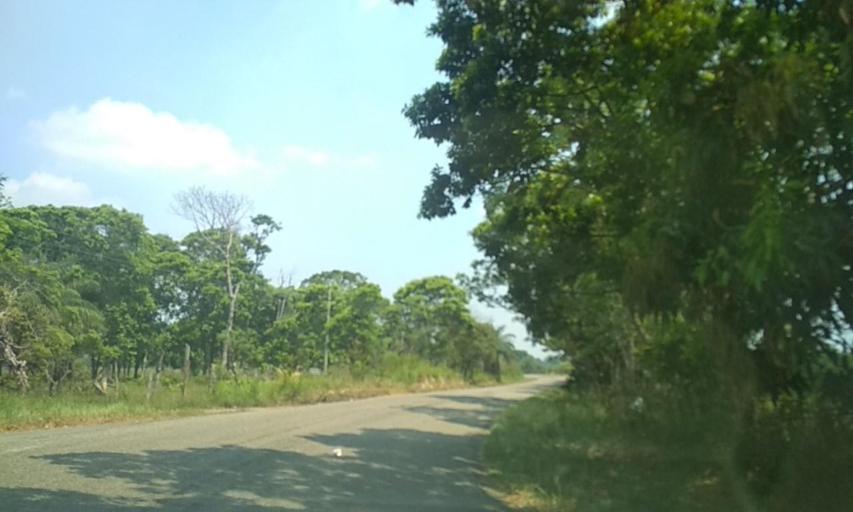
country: MX
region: Tabasco
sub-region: Huimanguillo
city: C-41 (Licenciado Carlos A. Madrazo)
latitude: 17.8497
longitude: -93.5289
